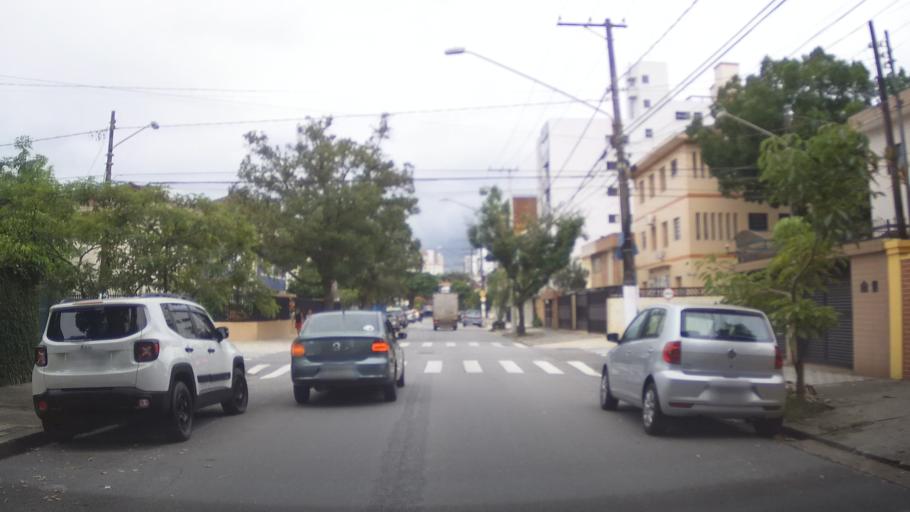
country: BR
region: Sao Paulo
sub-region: Santos
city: Santos
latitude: -23.9689
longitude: -46.3171
